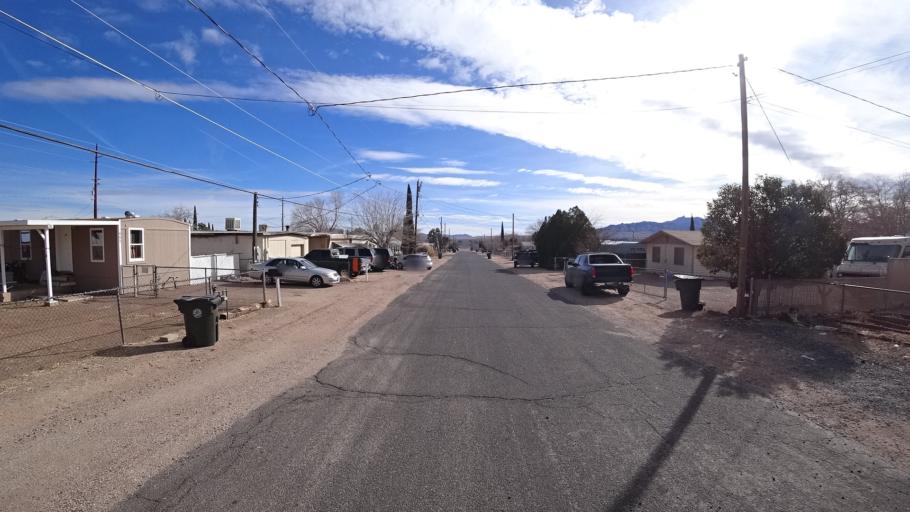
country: US
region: Arizona
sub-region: Mohave County
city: Kingman
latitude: 35.2164
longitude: -114.0521
